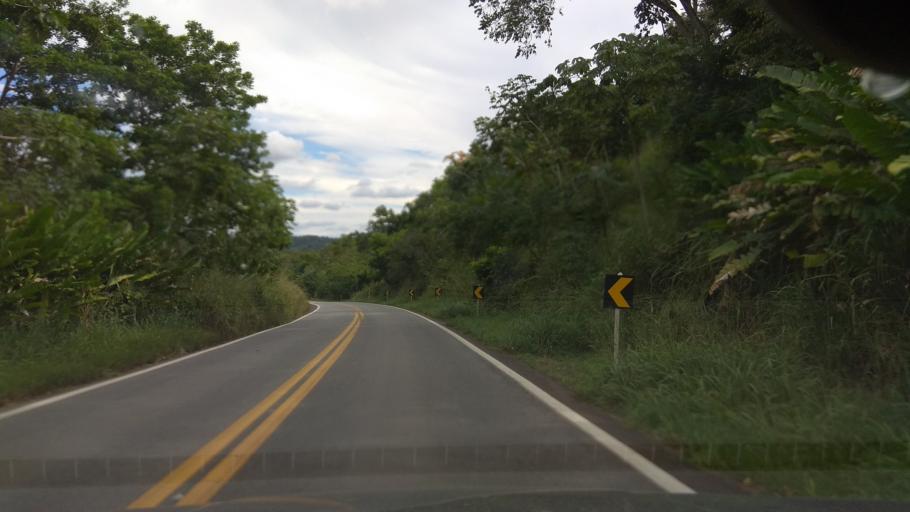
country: BR
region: Bahia
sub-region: Ubata
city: Ubata
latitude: -14.1981
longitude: -39.5674
